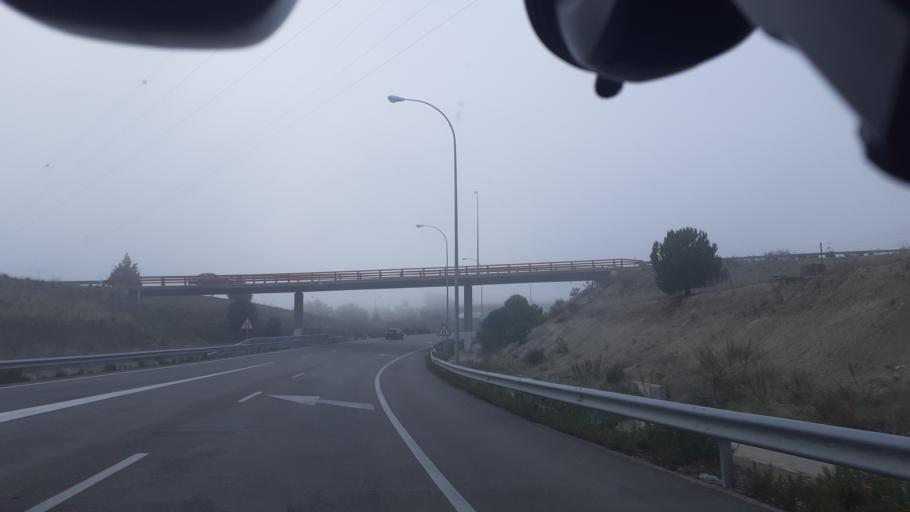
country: ES
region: Madrid
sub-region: Provincia de Madrid
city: Villa de Vallecas
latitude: 40.3754
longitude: -3.5980
